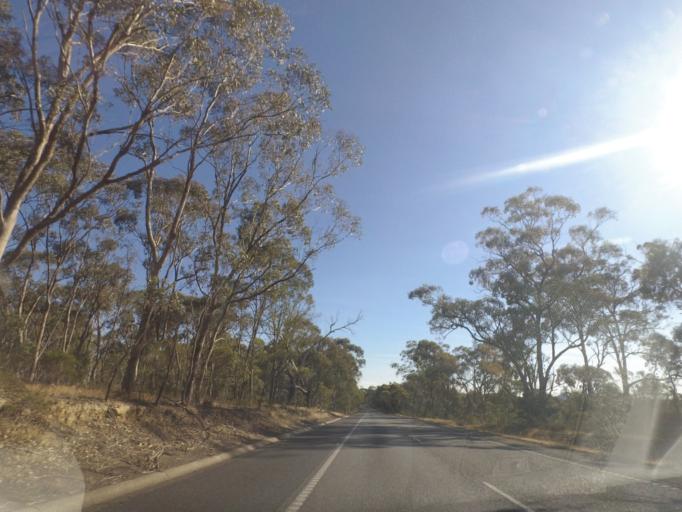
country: AU
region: Victoria
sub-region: Murrindindi
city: Kinglake West
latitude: -37.1754
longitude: 145.0727
